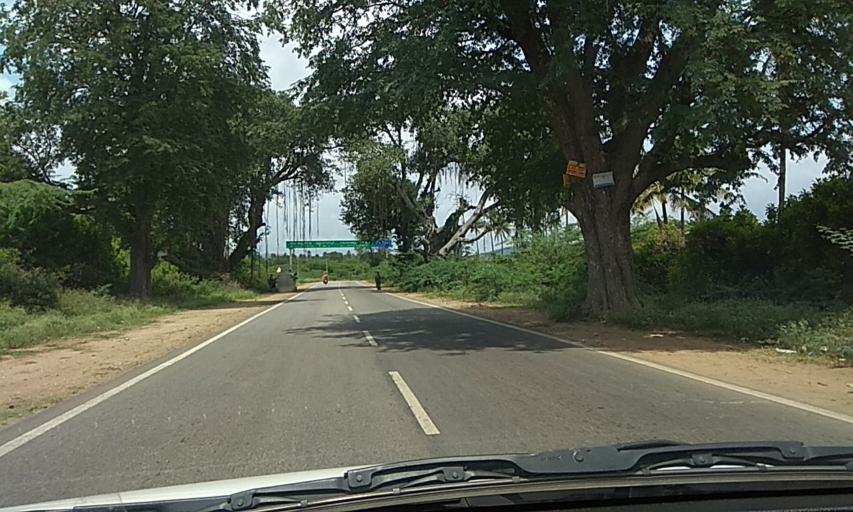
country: IN
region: Karnataka
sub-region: Chamrajnagar
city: Gundlupet
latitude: 11.8109
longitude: 76.7079
